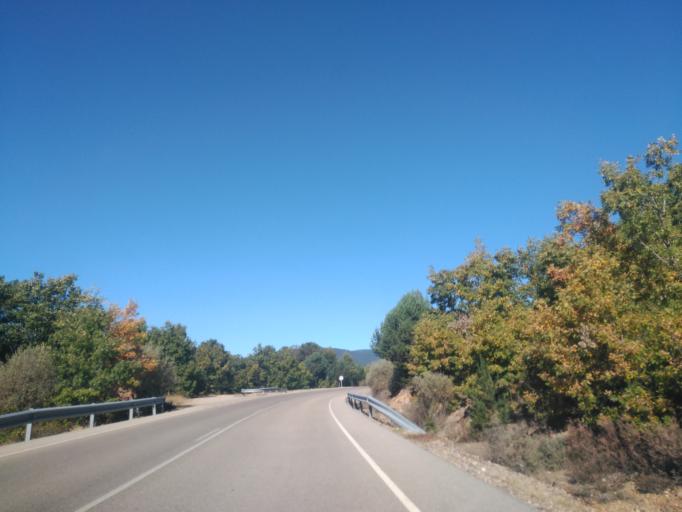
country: ES
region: Castille and Leon
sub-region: Provincia de Soria
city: Vinuesa
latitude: 41.8939
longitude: -2.7317
